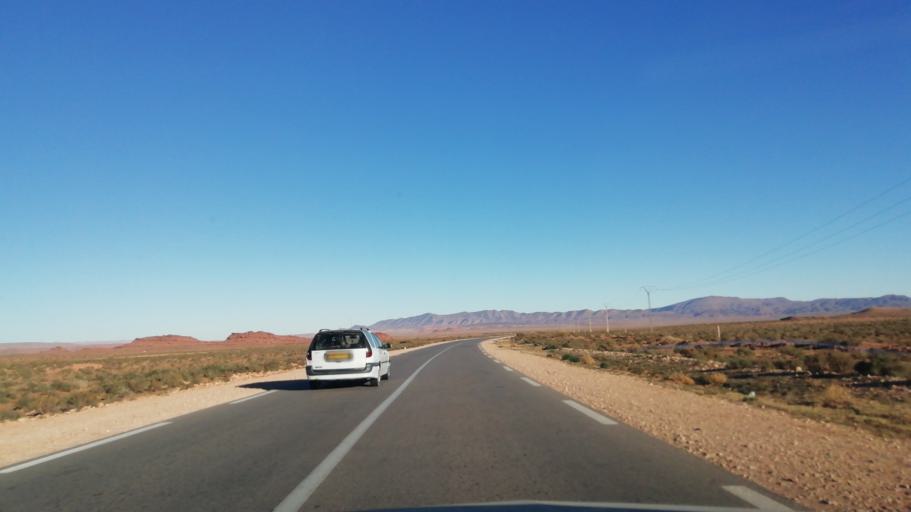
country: DZ
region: El Bayadh
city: El Abiodh Sidi Cheikh
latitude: 33.1706
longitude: 0.4913
